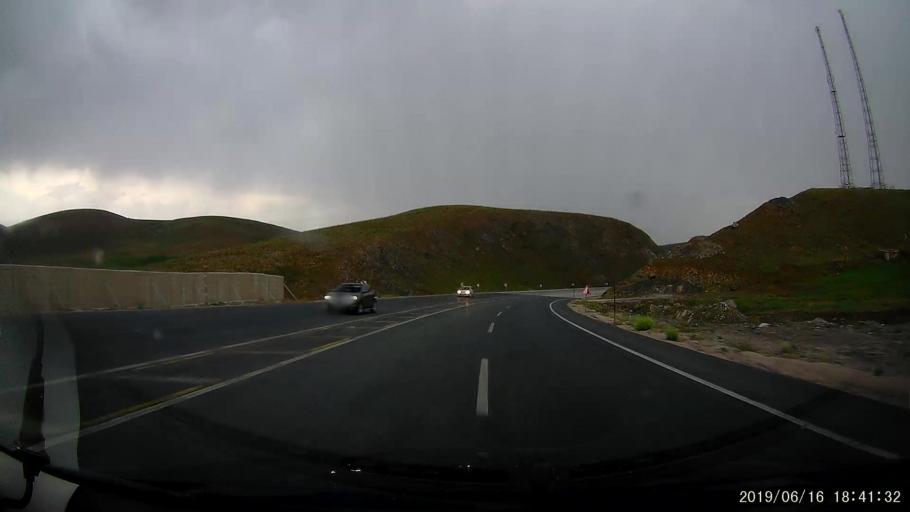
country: TR
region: Erzincan
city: Doganbeyli
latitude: 39.8722
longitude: 39.1271
